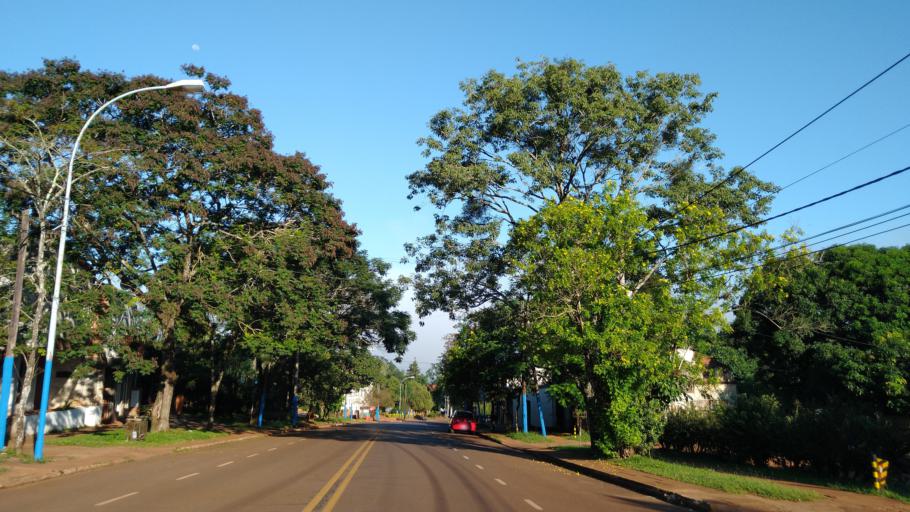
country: AR
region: Misiones
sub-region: Departamento de Montecarlo
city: Montecarlo
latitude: -26.5662
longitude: -54.7693
